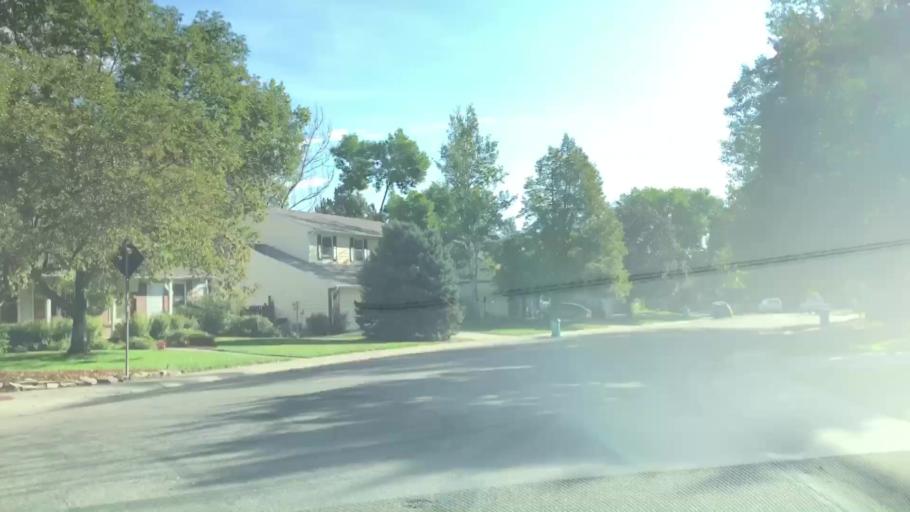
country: US
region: Colorado
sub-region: Larimer County
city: Fort Collins
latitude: 40.5281
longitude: -105.0474
